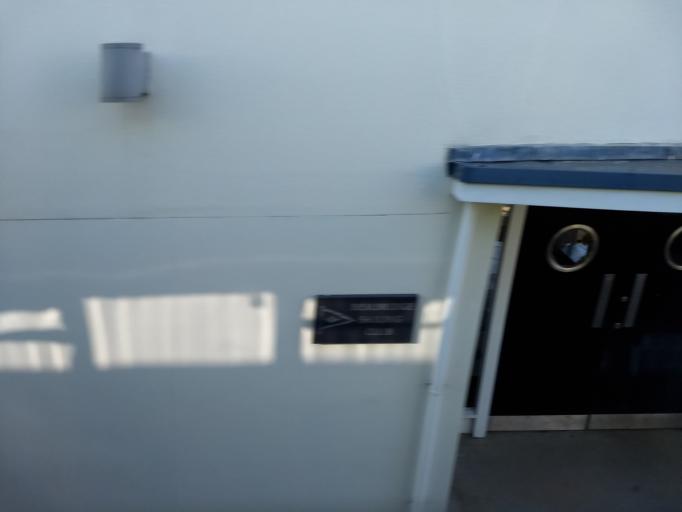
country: GB
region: England
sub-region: Isle of Wight
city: Bembridge
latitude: 50.6933
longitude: -1.0929
